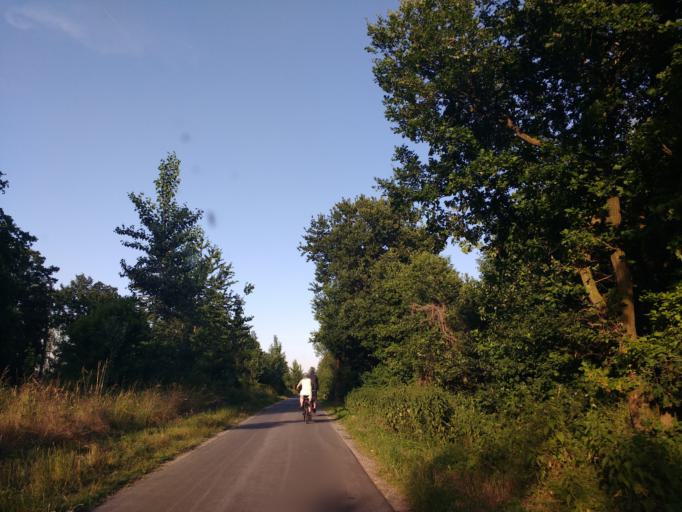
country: DE
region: North Rhine-Westphalia
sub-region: Regierungsbezirk Arnsberg
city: Lippstadt
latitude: 51.7207
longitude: 8.4187
